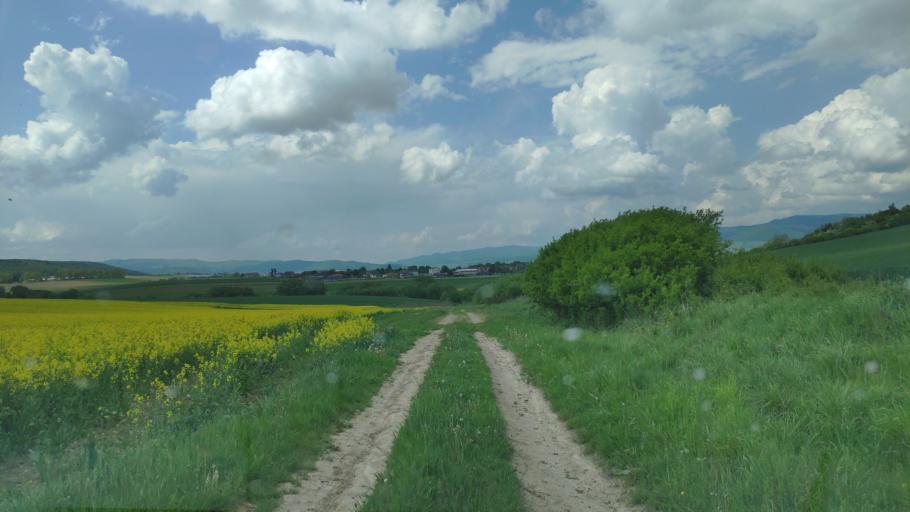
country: SK
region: Presovsky
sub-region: Okres Presov
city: Presov
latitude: 49.0316
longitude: 21.1657
